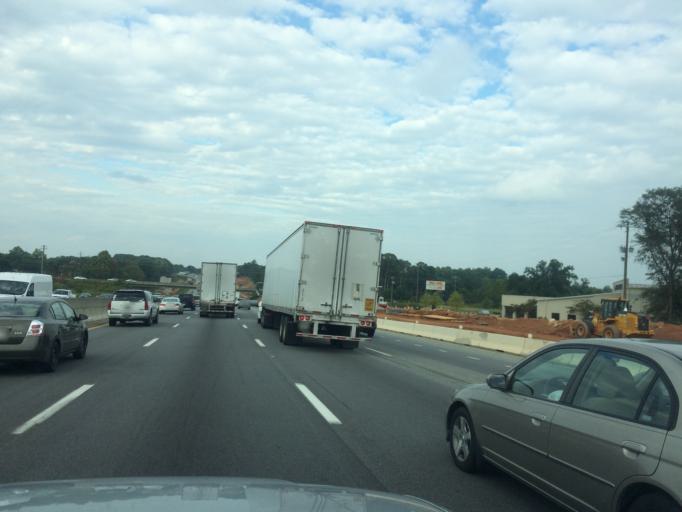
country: US
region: South Carolina
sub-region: Greenville County
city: Mauldin
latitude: 34.8365
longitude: -82.2910
